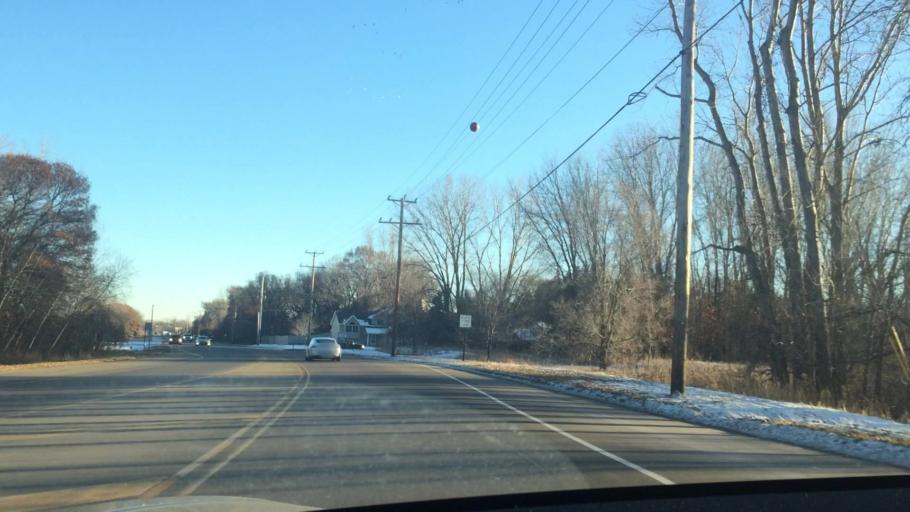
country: US
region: Minnesota
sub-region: Anoka County
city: Circle Pines
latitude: 45.1497
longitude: -93.1350
